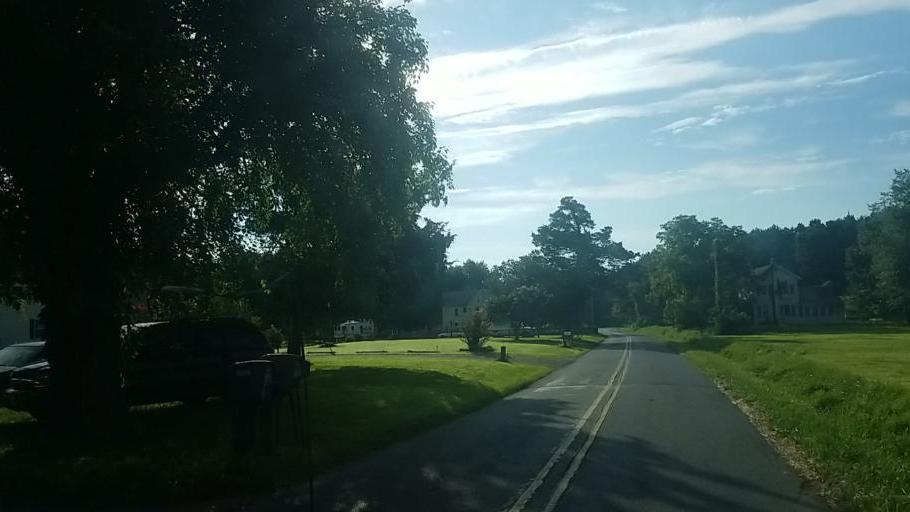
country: US
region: Maryland
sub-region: Worcester County
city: Berlin
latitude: 38.3132
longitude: -75.1613
